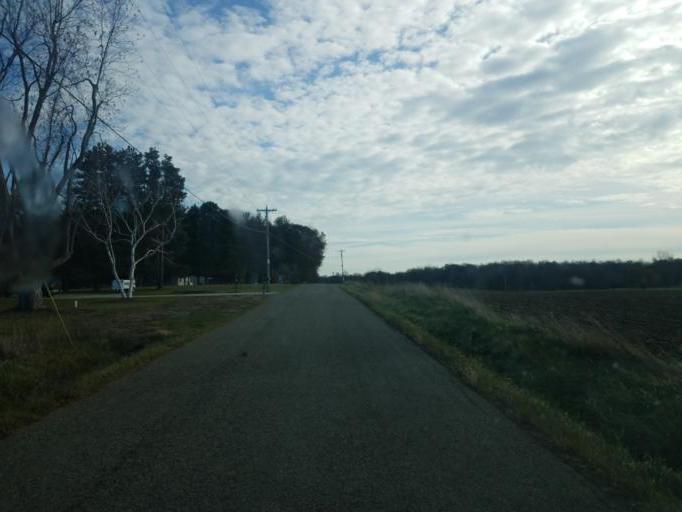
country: US
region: Ohio
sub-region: Crawford County
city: Crestline
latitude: 40.7175
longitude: -82.6752
